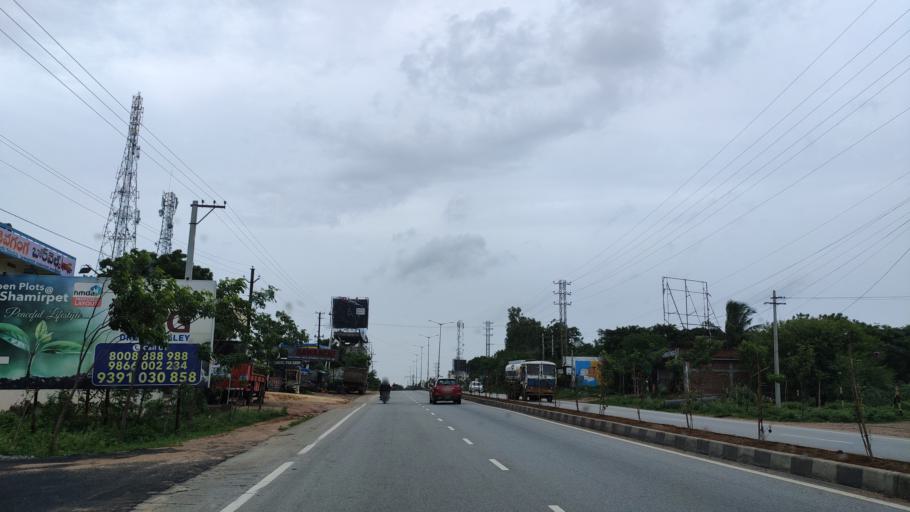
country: IN
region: Telangana
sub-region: Rangareddi
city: Secunderabad
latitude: 17.5922
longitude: 78.5704
